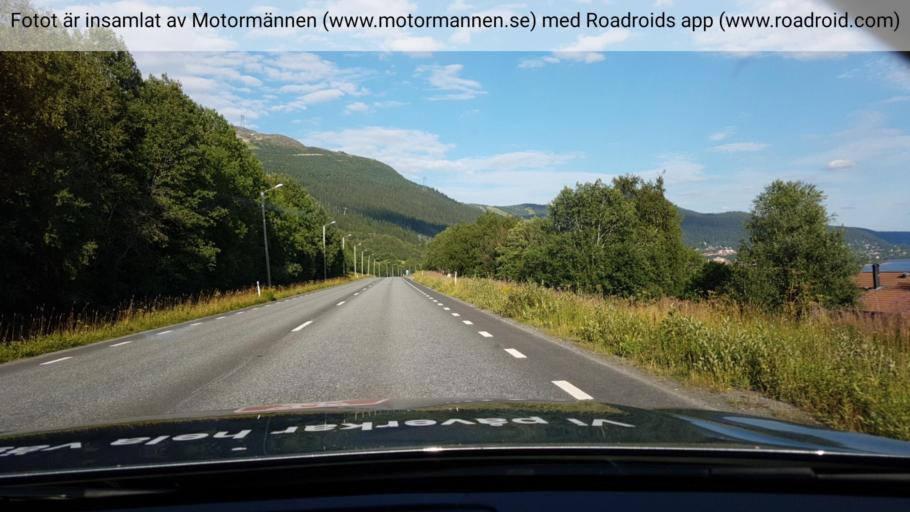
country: SE
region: Jaemtland
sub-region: Are Kommun
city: Are
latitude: 63.4051
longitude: 13.0306
